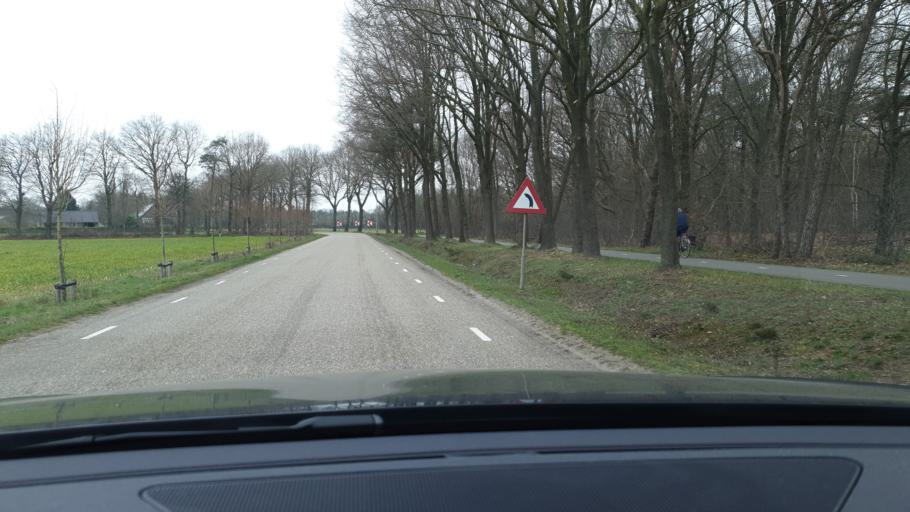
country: NL
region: North Brabant
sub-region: Gemeente Eersel
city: Eersel
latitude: 51.4136
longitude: 5.3051
